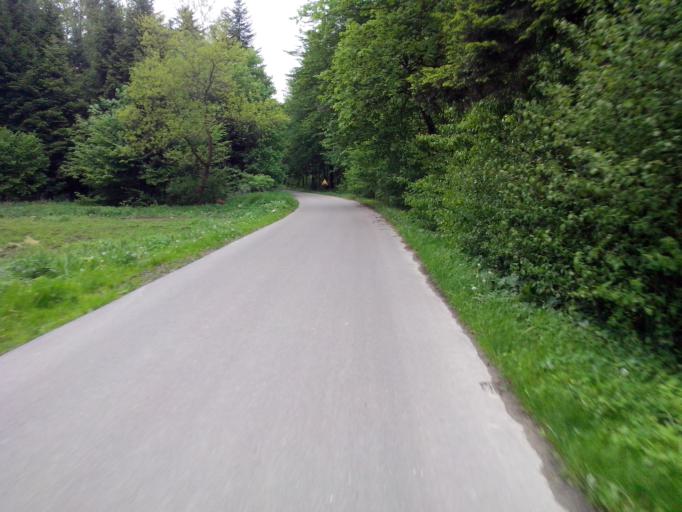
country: PL
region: Subcarpathian Voivodeship
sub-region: Powiat strzyzowski
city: Strzyzow
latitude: 49.8053
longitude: 21.8276
